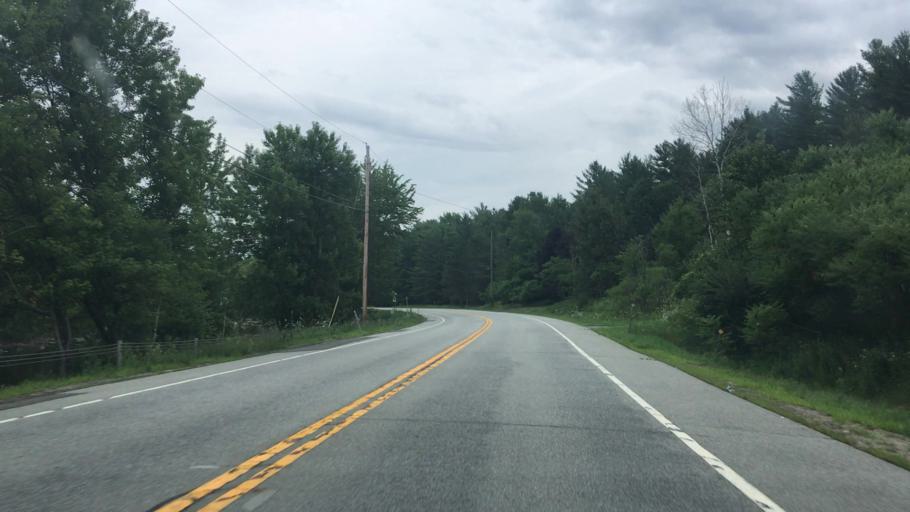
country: US
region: New York
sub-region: Essex County
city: Lake Placid
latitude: 44.3182
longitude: -73.7819
